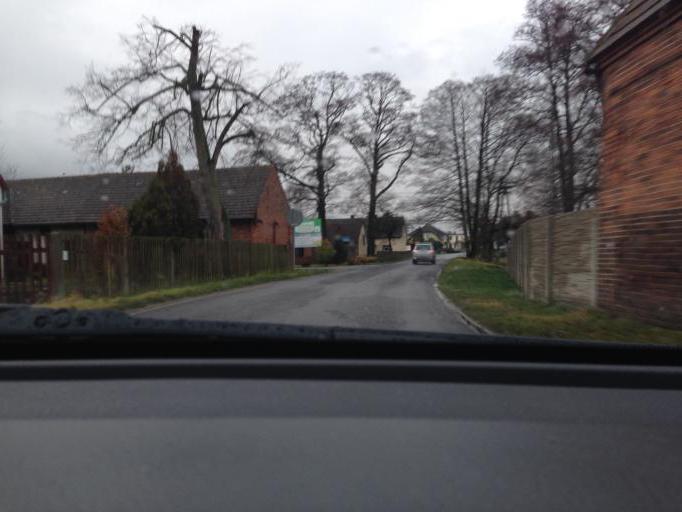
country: PL
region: Opole Voivodeship
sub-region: Powiat opolski
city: Wegry
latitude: 50.7255
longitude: 18.0739
